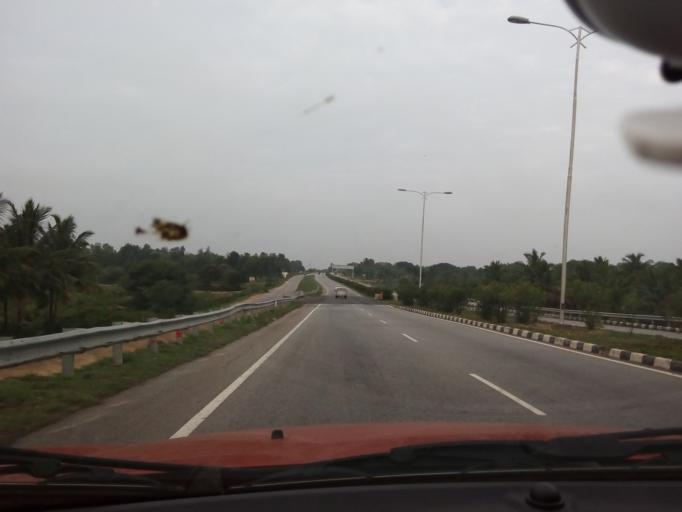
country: IN
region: Karnataka
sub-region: Tumkur
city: Kunigal
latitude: 13.0030
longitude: 76.9526
